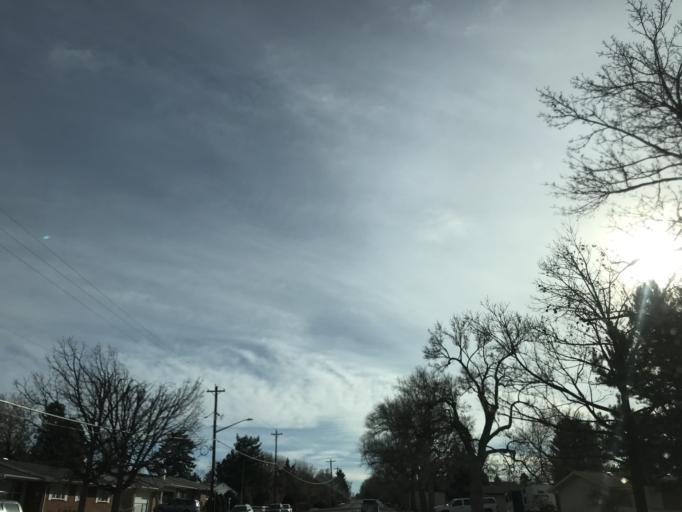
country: US
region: Colorado
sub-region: Arapahoe County
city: Littleton
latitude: 39.5991
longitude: -105.0131
